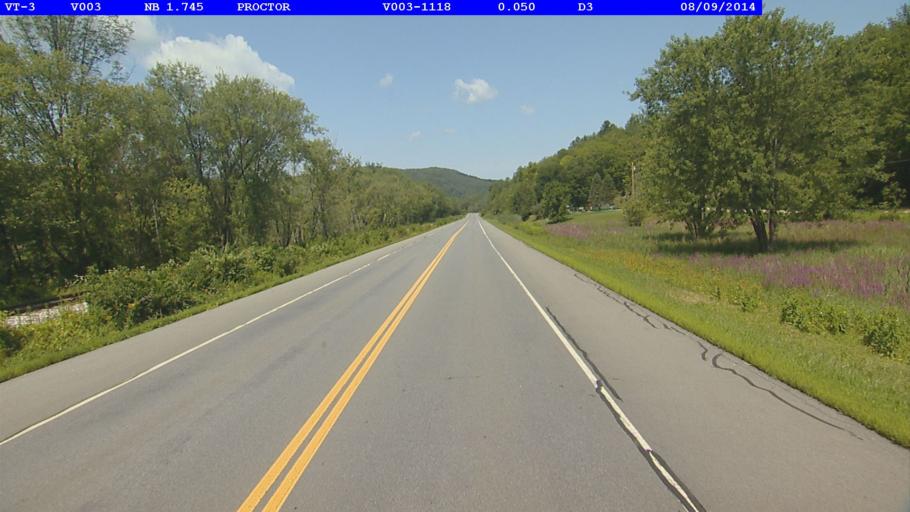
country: US
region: Vermont
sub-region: Rutland County
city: West Rutland
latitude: 43.6259
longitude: -73.0290
